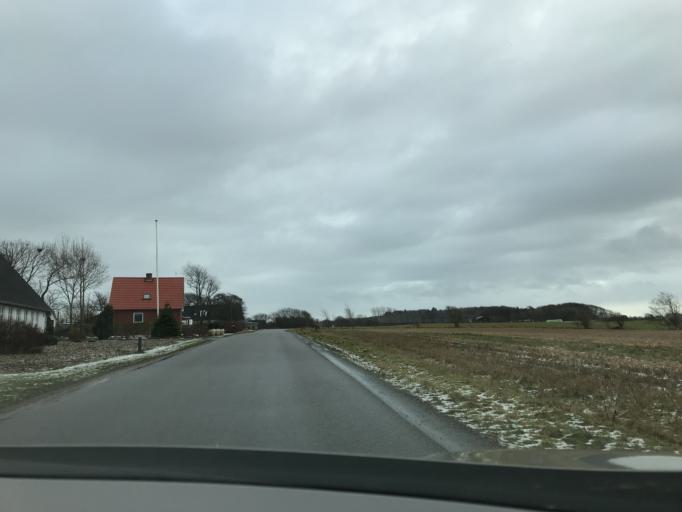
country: DK
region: South Denmark
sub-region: Varde Kommune
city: Varde
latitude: 55.6529
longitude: 8.4416
